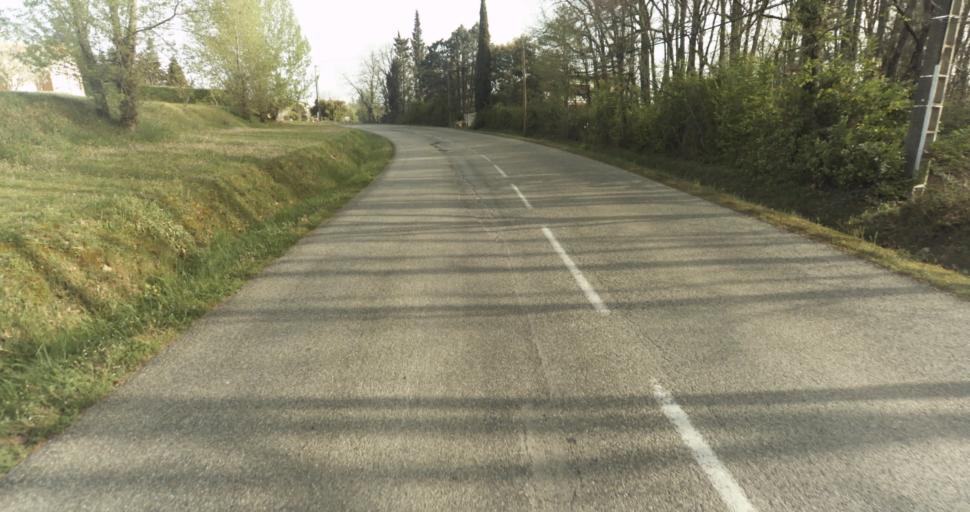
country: FR
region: Midi-Pyrenees
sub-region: Departement du Tarn-et-Garonne
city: Moissac
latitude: 44.1515
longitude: 1.0988
